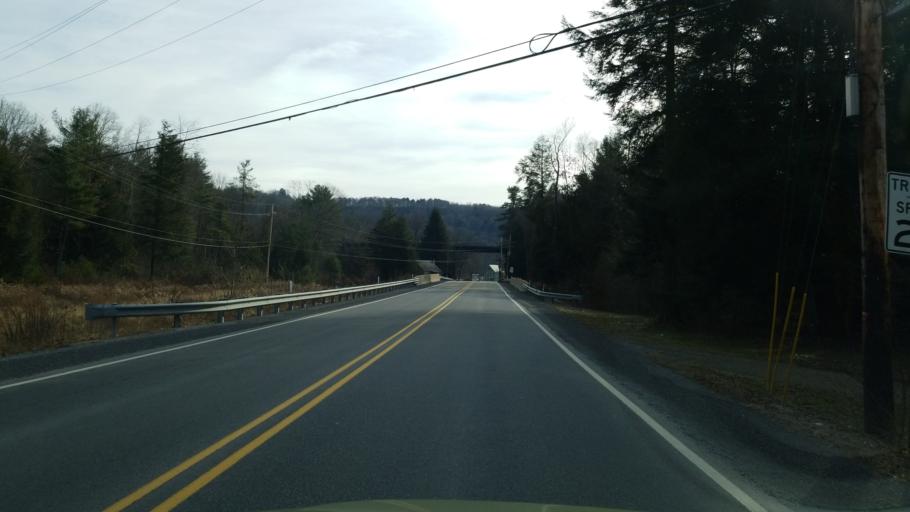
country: US
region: Pennsylvania
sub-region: Indiana County
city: Johnsonburg
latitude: 40.8843
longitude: -78.7660
